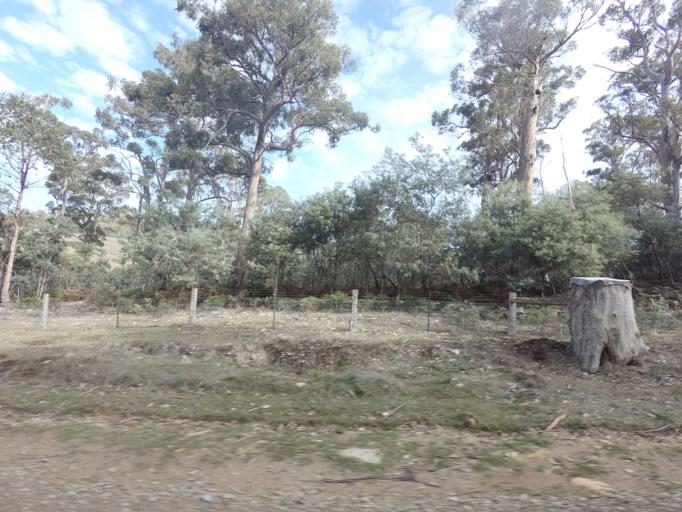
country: AU
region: Tasmania
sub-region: Sorell
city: Sorell
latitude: -42.5641
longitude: 147.4684
